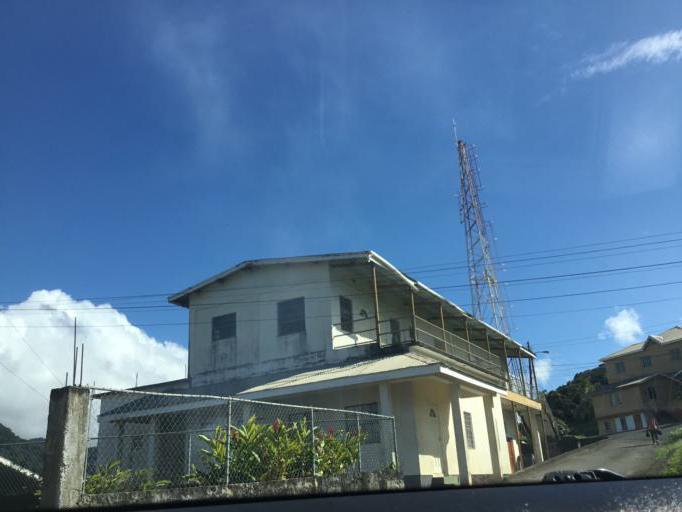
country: VC
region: Saint David
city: Chateaubelair
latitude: 13.2709
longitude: -61.2388
